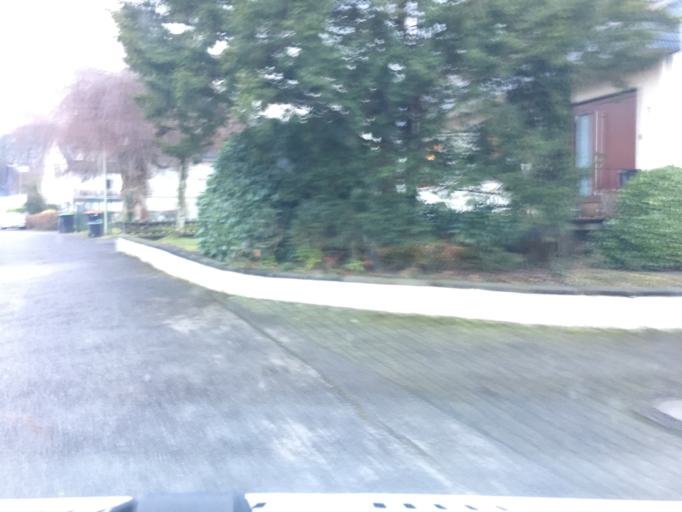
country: DE
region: North Rhine-Westphalia
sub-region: Regierungsbezirk Koln
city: Odenthal
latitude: 51.0169
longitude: 7.1145
